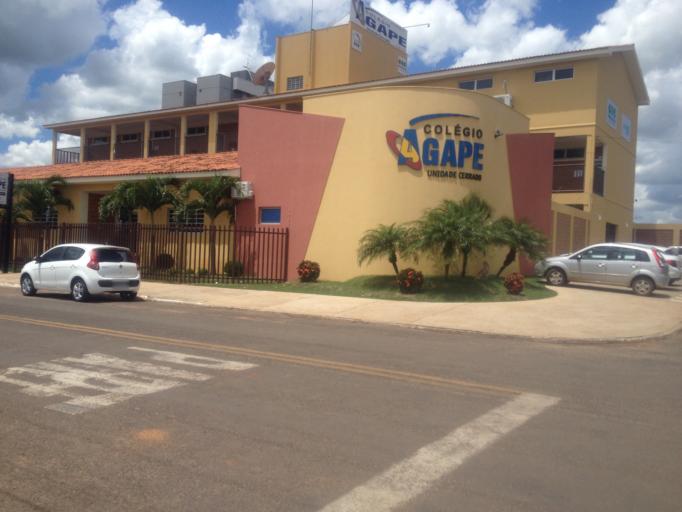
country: BR
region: Goias
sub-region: Mineiros
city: Mineiros
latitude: -17.5593
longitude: -52.5639
